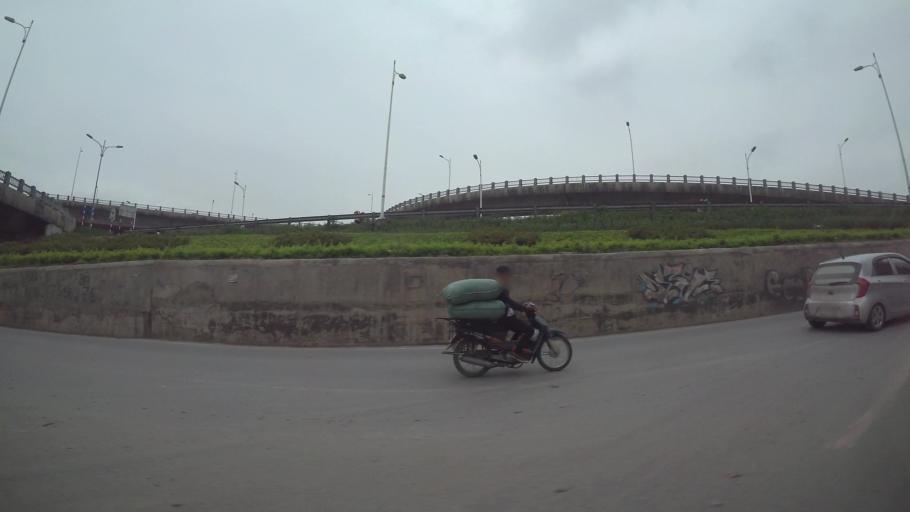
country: VN
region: Ha Noi
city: Hai BaTrung
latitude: 21.0018
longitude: 105.8751
